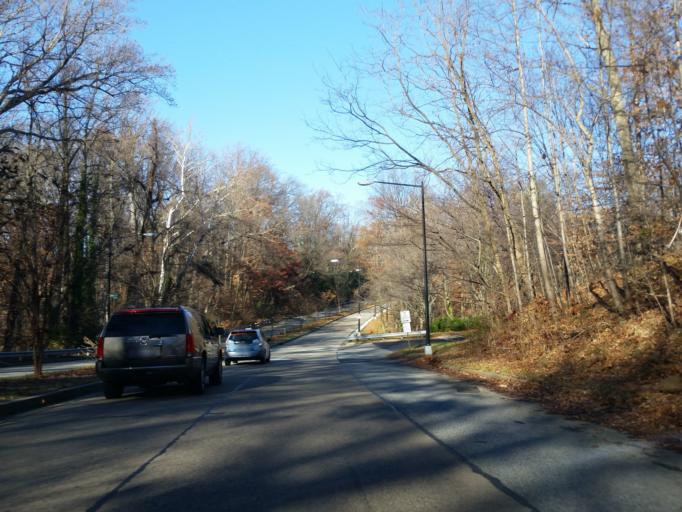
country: US
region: Maryland
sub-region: Montgomery County
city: Brookmont
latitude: 38.9448
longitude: -77.1035
